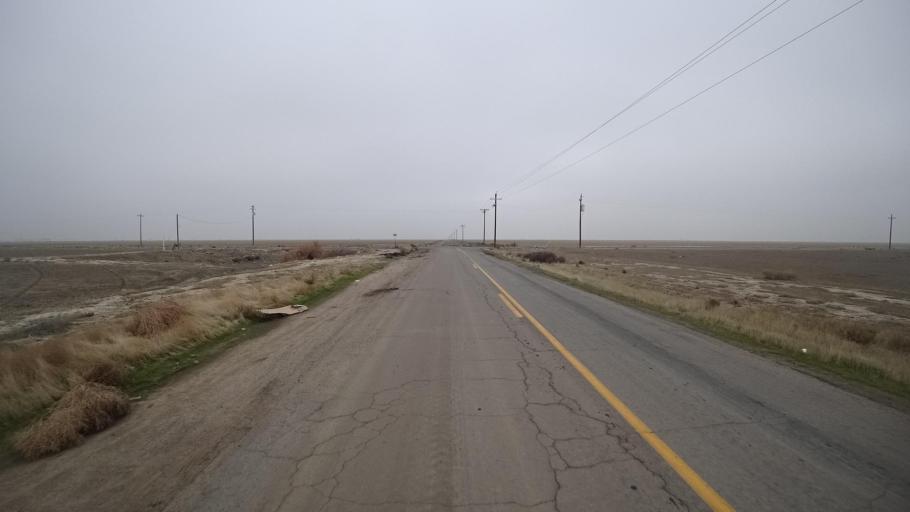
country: US
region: California
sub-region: Tulare County
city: Alpaugh
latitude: 35.7173
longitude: -119.4897
